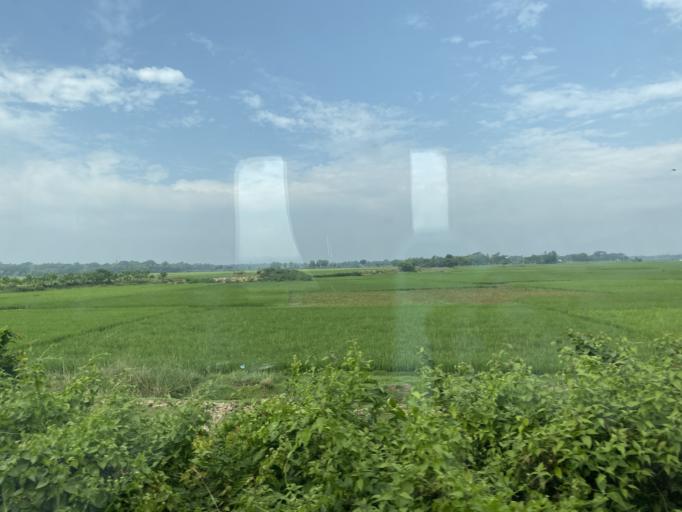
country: IN
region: Tripura
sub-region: West Tripura
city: Agartala
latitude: 23.9919
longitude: 91.2858
